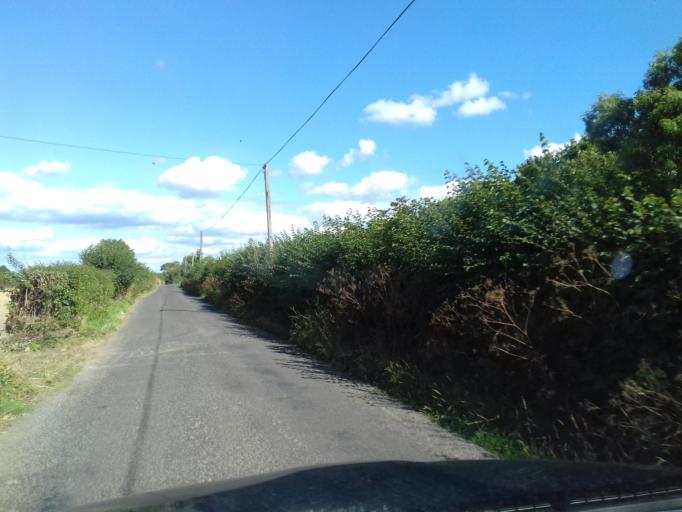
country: IE
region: Leinster
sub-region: Kilkenny
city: Callan
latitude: 52.5346
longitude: -7.3402
